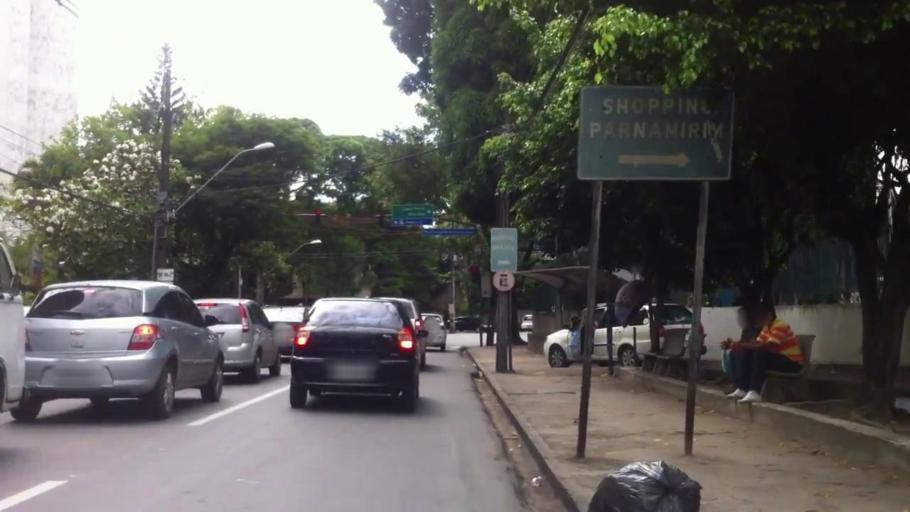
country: BR
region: Pernambuco
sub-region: Recife
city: Recife
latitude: -8.0362
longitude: -34.9069
